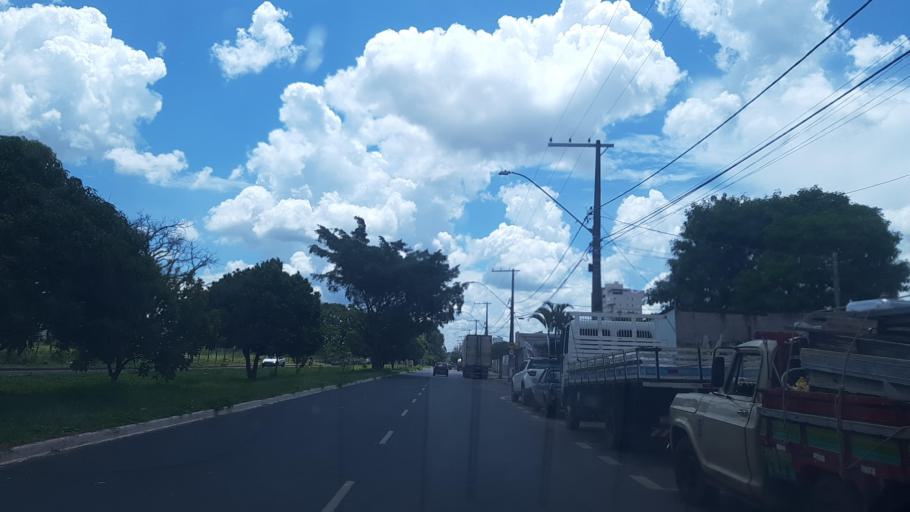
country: BR
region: Minas Gerais
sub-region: Uberlandia
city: Uberlandia
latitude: -18.9491
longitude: -48.3158
